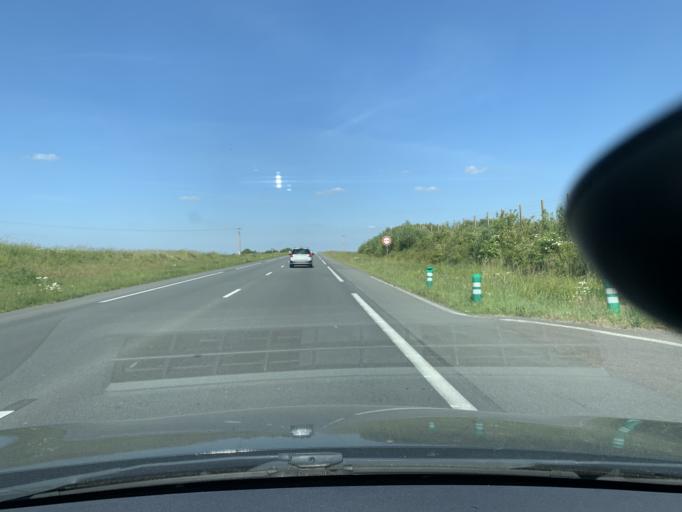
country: FR
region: Nord-Pas-de-Calais
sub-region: Departement du Nord
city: Cambrai
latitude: 50.1453
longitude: 3.2314
